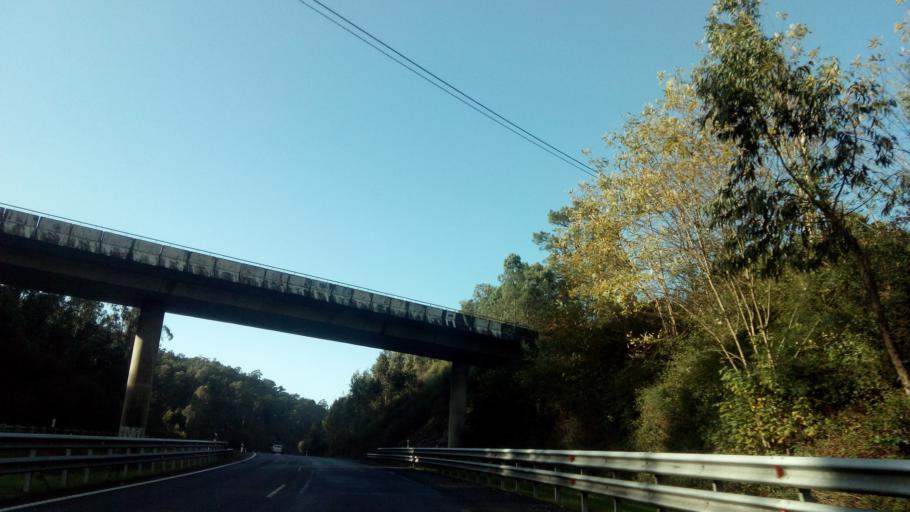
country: ES
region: Galicia
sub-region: Provincia de Pontevedra
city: Ponteareas
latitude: 42.1659
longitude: -8.5355
